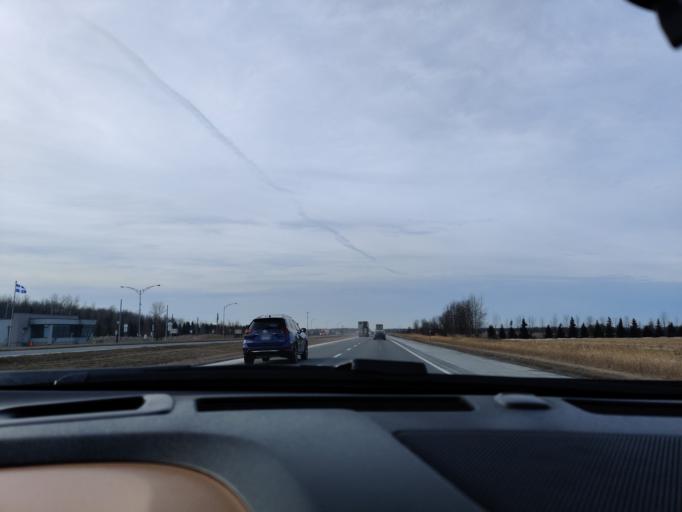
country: CA
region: Quebec
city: Les Cedres
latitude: 45.3350
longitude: -74.1016
